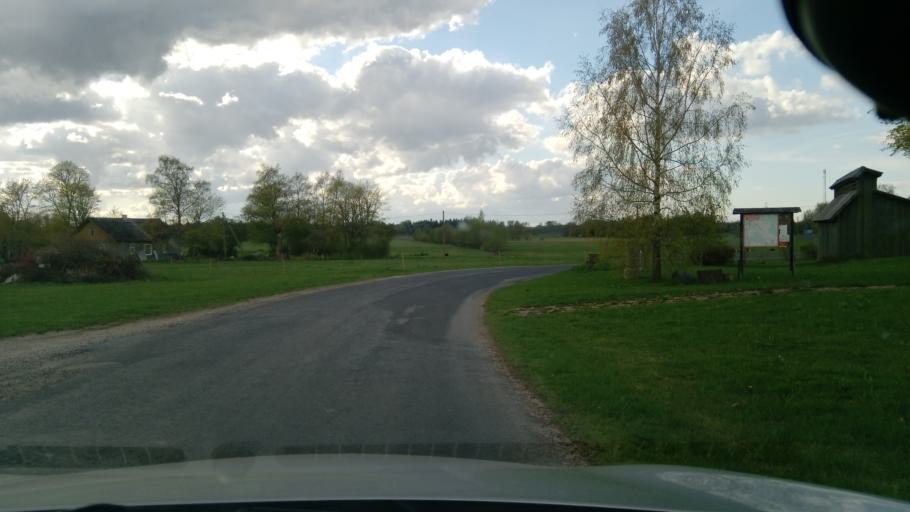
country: EE
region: Jaervamaa
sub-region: Jaerva-Jaani vald
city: Jarva-Jaani
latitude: 59.0122
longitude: 25.7372
